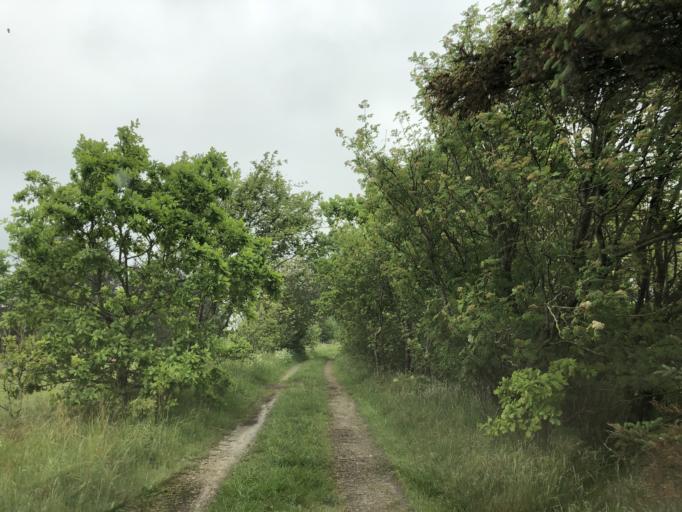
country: DK
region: Central Jutland
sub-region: Holstebro Kommune
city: Holstebro
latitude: 56.3337
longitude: 8.4806
